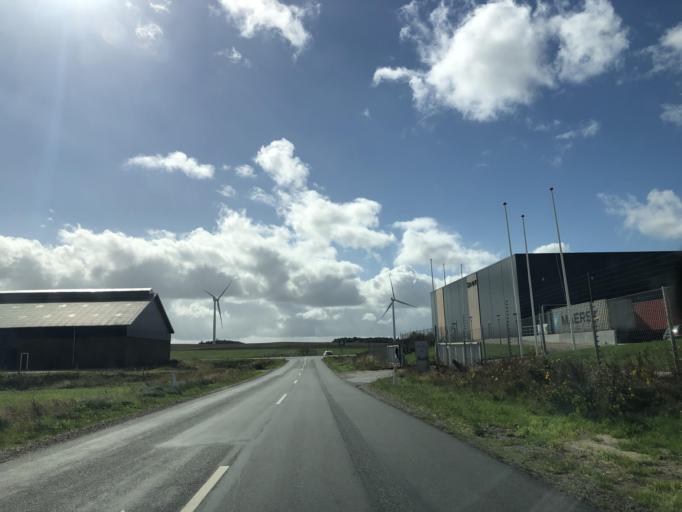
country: DK
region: North Denmark
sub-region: Mariagerfjord Kommune
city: Mariager
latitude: 56.5407
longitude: 9.8973
